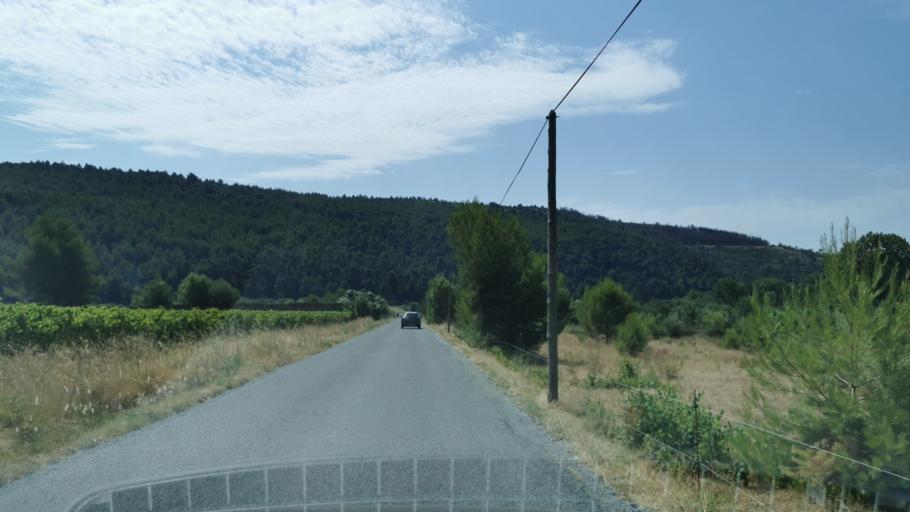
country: FR
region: Languedoc-Roussillon
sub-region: Departement de l'Aude
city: Bize-Minervois
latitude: 43.3262
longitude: 2.8789
